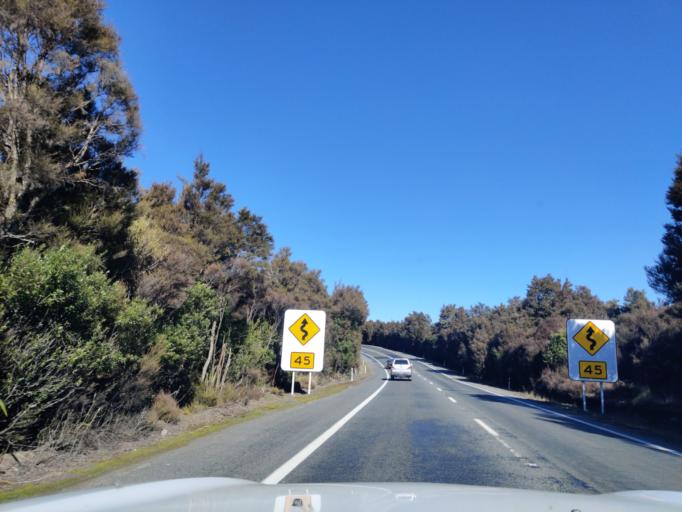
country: NZ
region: Waikato
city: Turangi
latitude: -39.1761
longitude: 175.7689
